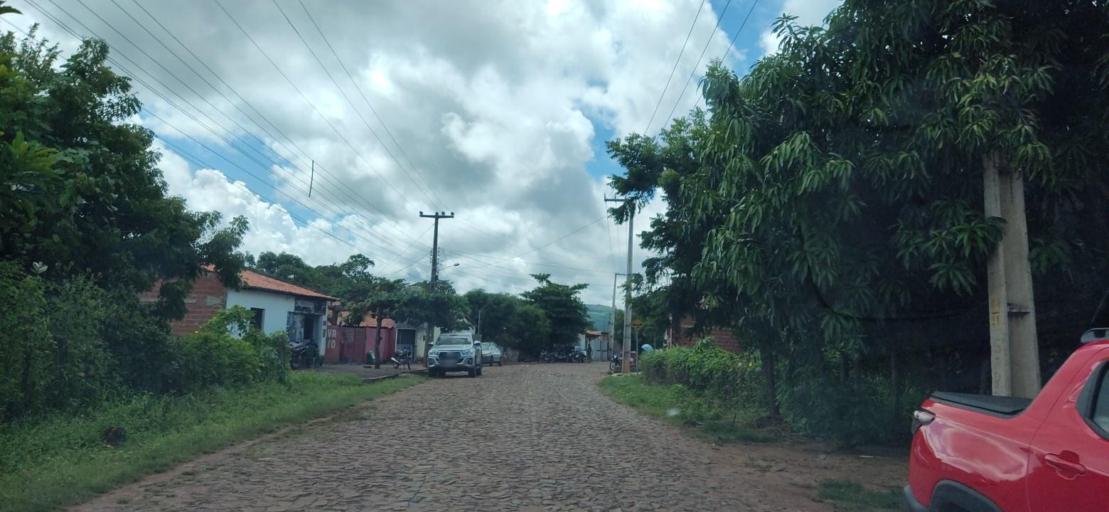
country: BR
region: Piaui
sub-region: Valenca Do Piaui
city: Valenca do Piaui
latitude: -6.1113
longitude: -41.7993
